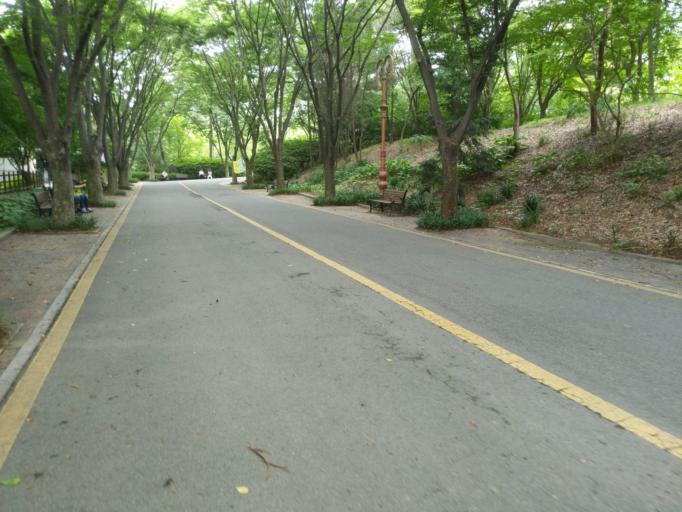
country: KR
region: Daegu
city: Hwawon
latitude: 35.8009
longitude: 128.5219
